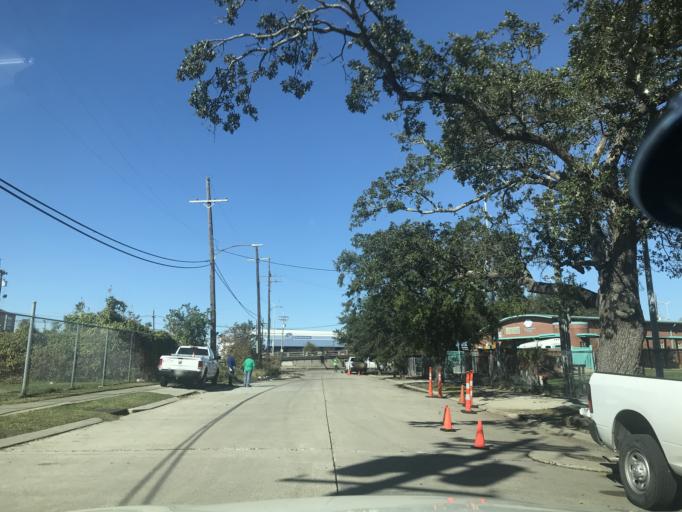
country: US
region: Louisiana
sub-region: Orleans Parish
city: New Orleans
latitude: 29.9536
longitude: -90.0962
